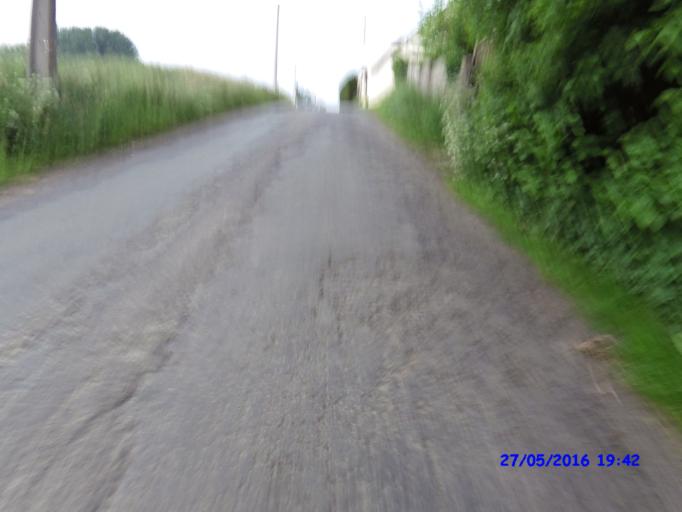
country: BE
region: Flanders
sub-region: Provincie Oost-Vlaanderen
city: Denderleeuw
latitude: 50.9252
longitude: 4.1273
